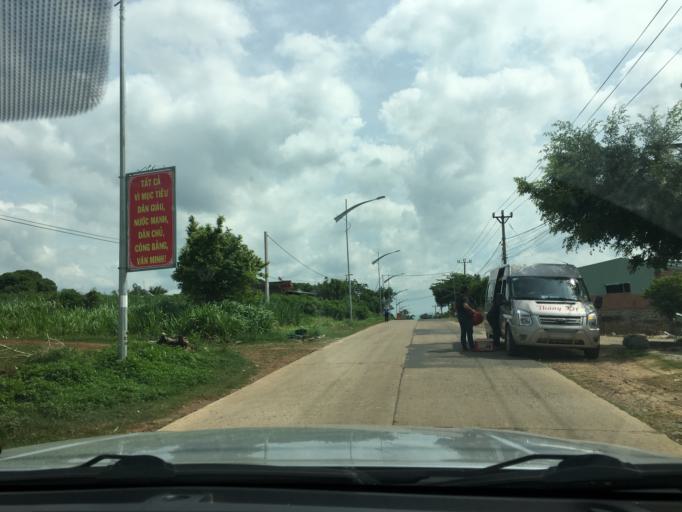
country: VN
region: Gia Lai
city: Kong Chro
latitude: 13.7812
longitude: 108.5181
